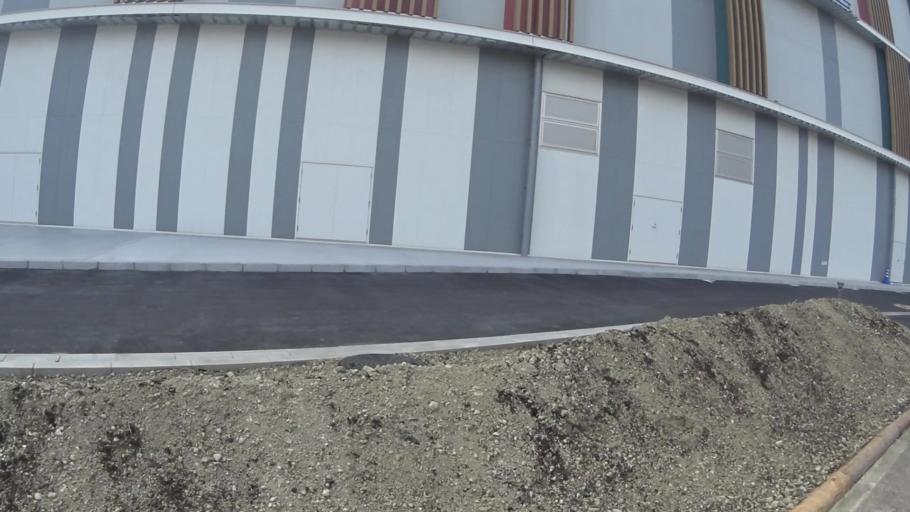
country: JP
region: Kyoto
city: Muko
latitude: 34.9641
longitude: 135.7078
